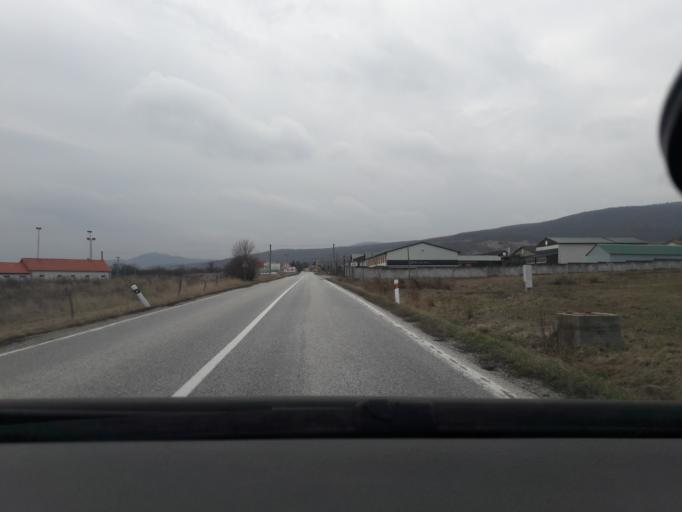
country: SK
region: Trnavsky
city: Smolenice
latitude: 48.4182
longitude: 17.3856
